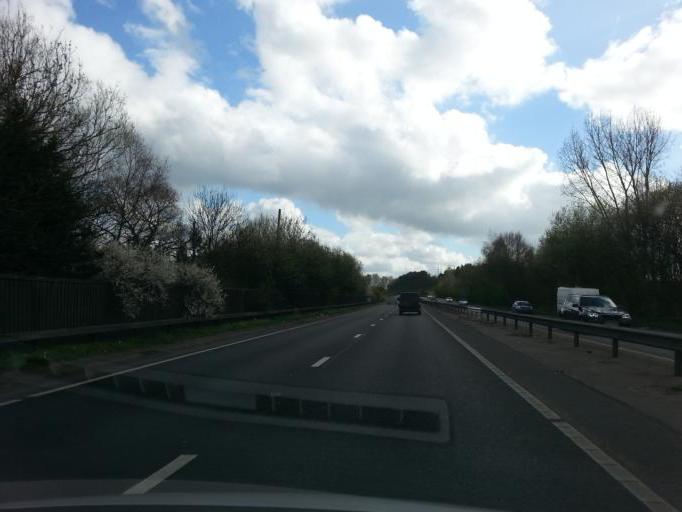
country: GB
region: England
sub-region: Hampshire
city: Aldershot
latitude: 51.2666
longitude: -0.7349
